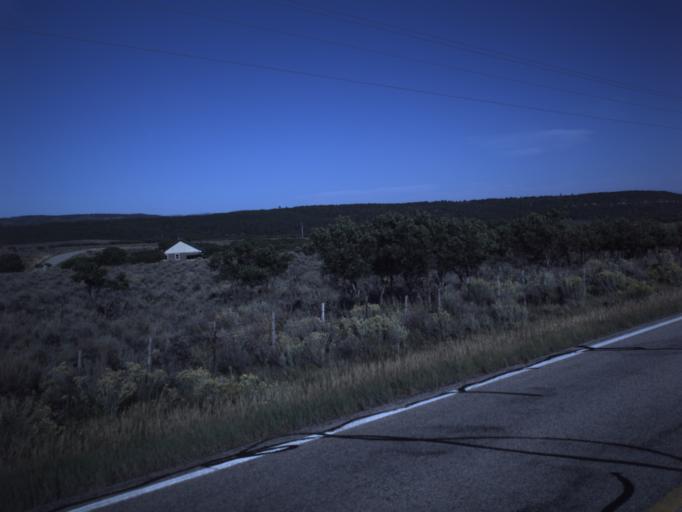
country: US
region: Utah
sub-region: Grand County
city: Moab
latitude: 38.3402
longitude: -109.1697
